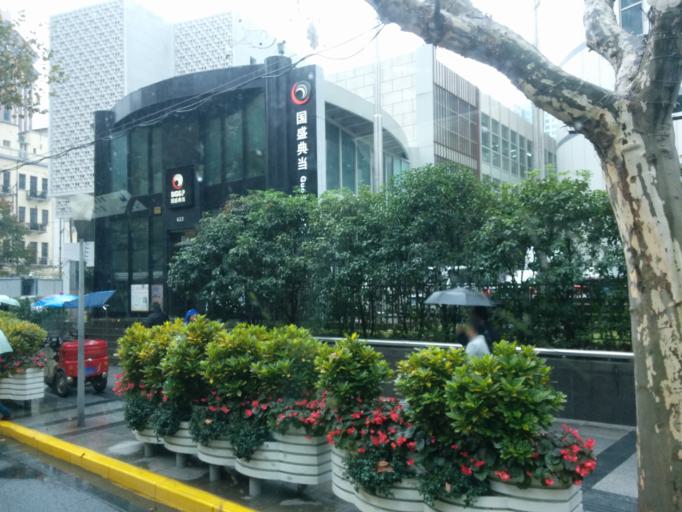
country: CN
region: Shanghai Shi
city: Shanghai
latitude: 31.2326
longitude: 121.4606
